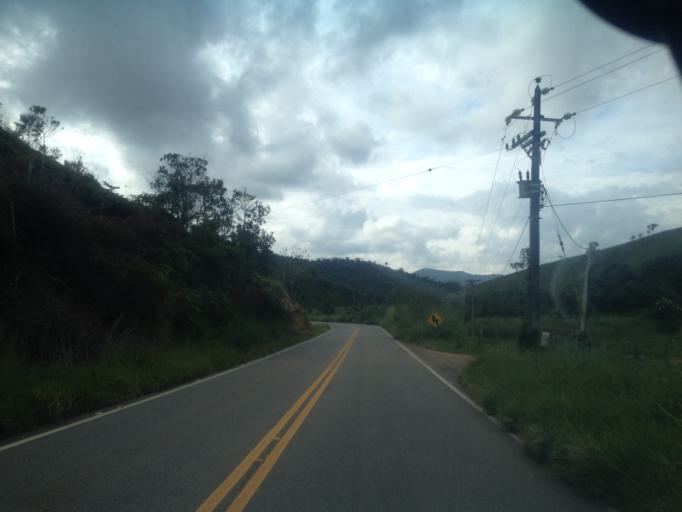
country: BR
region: Rio de Janeiro
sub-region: Quatis
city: Quatis
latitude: -22.3756
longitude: -44.2621
